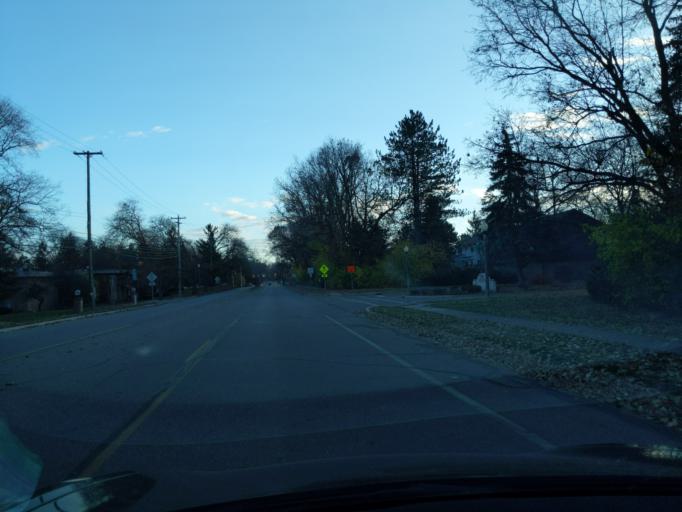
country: US
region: Michigan
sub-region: Ingham County
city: East Lansing
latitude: 42.7471
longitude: -84.4936
